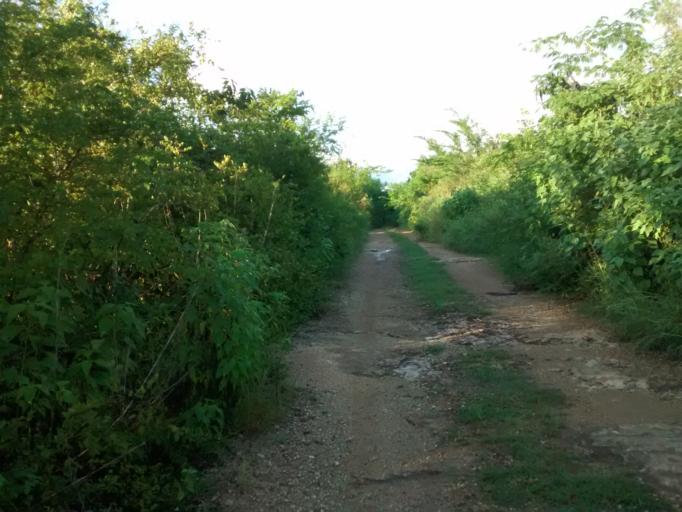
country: MX
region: Yucatan
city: Valladolid
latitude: 20.7156
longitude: -88.2064
